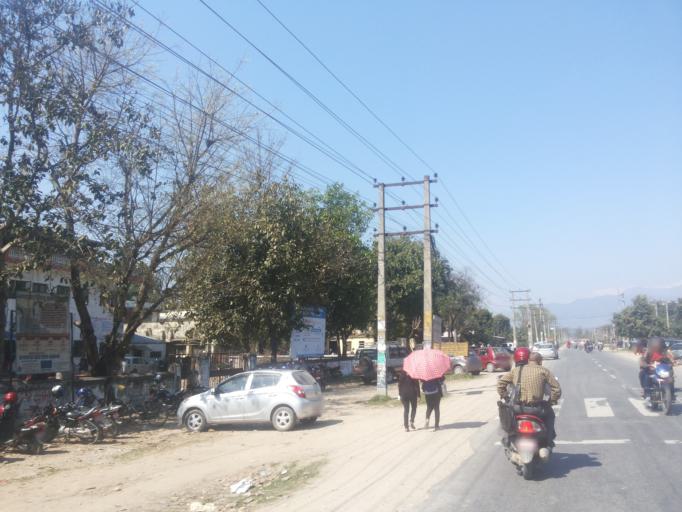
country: NP
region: Central Region
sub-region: Narayani Zone
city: Bharatpur
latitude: 27.6803
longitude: 84.4393
